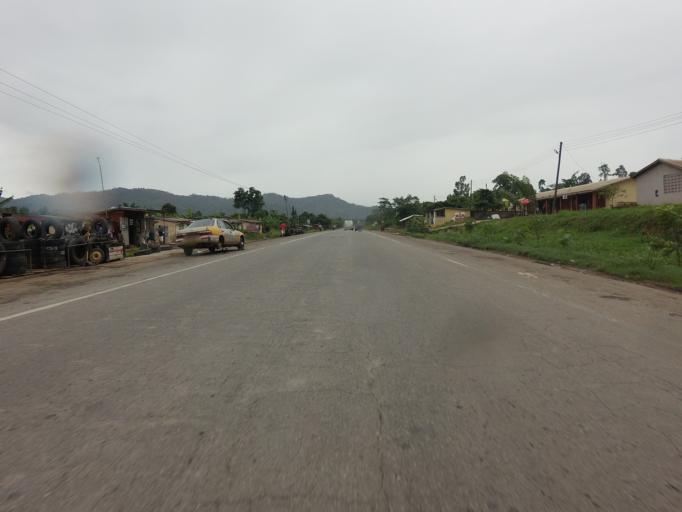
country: GH
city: Kibi
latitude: 6.1159
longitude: -0.4908
